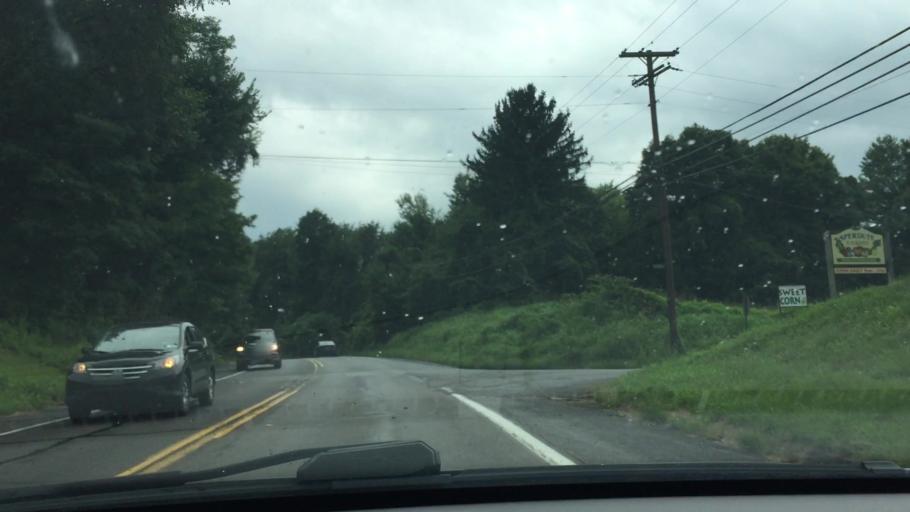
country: US
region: Pennsylvania
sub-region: Lawrence County
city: Oakland
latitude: 40.9669
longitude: -80.4243
